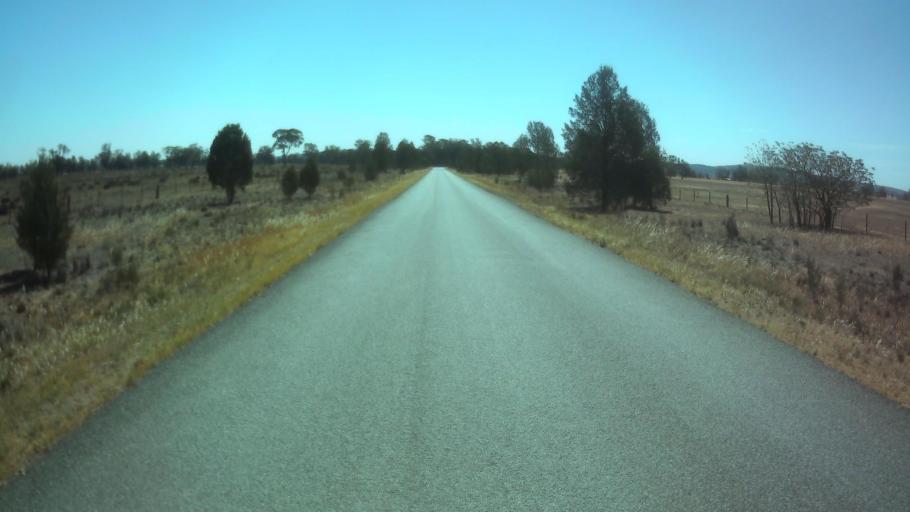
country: AU
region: New South Wales
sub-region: Weddin
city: Grenfell
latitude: -33.8158
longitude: 147.9378
